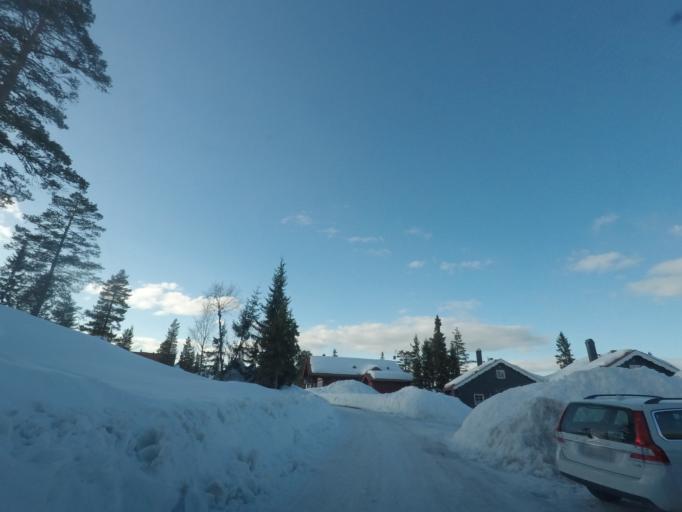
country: SE
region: Dalarna
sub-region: Malung-Saelens kommun
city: Malung
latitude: 61.1724
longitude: 13.1893
